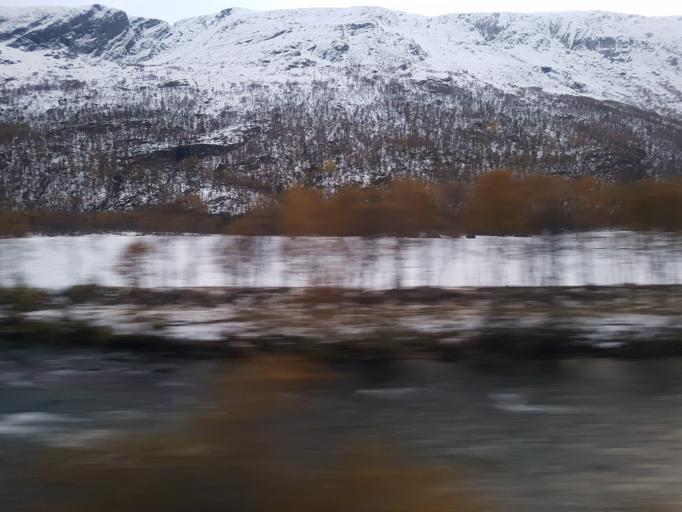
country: NO
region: Sor-Trondelag
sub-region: Oppdal
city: Oppdal
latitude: 62.4156
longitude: 9.6212
